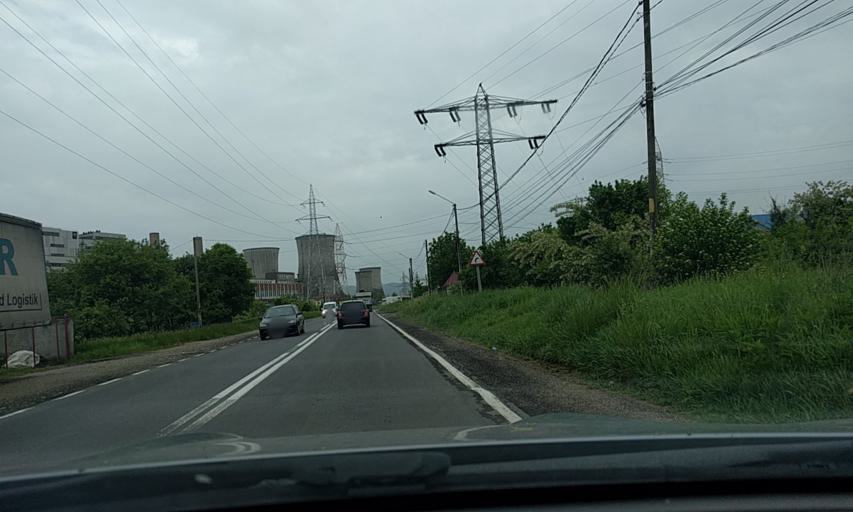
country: RO
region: Dambovita
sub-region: Comuna Doicesti
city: Doicesti
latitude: 44.9981
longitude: 25.4024
